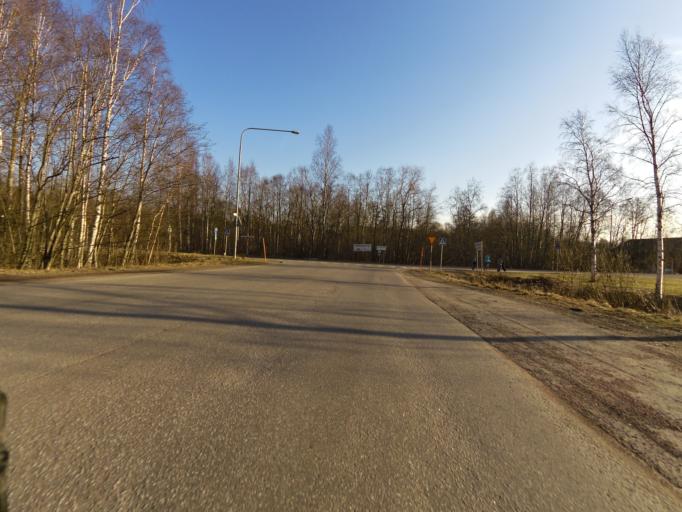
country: SE
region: Gaevleborg
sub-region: Gavle Kommun
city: Gavle
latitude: 60.6723
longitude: 17.2012
